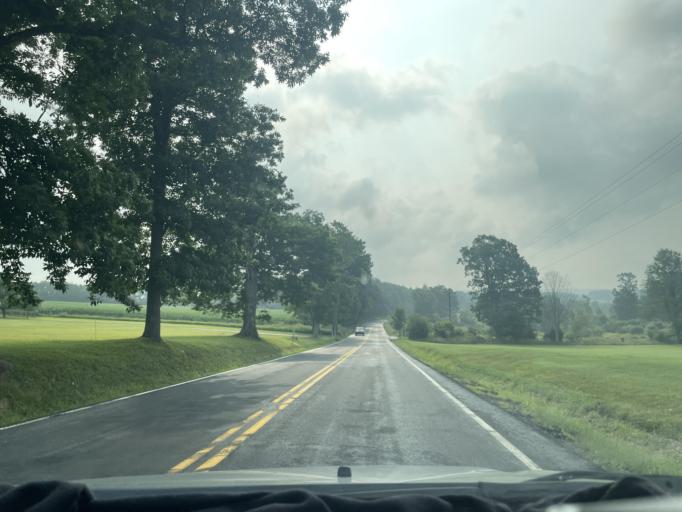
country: US
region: Maryland
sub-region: Garrett County
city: Mountain Lake Park
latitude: 39.2984
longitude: -79.3814
